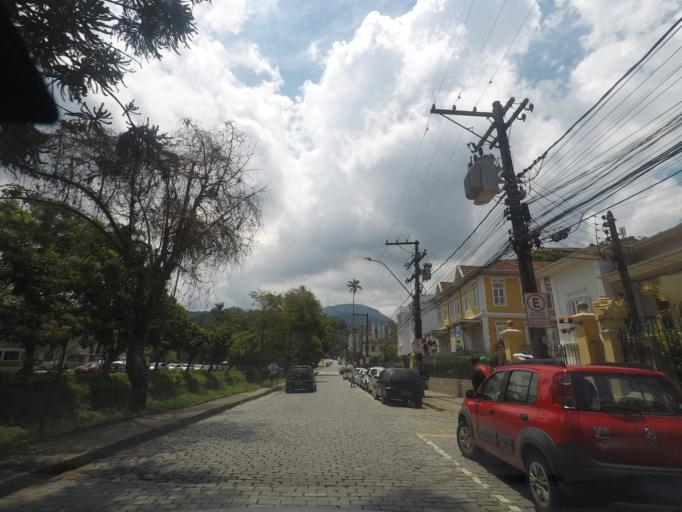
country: BR
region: Rio de Janeiro
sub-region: Petropolis
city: Petropolis
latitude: -22.5073
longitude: -43.1769
